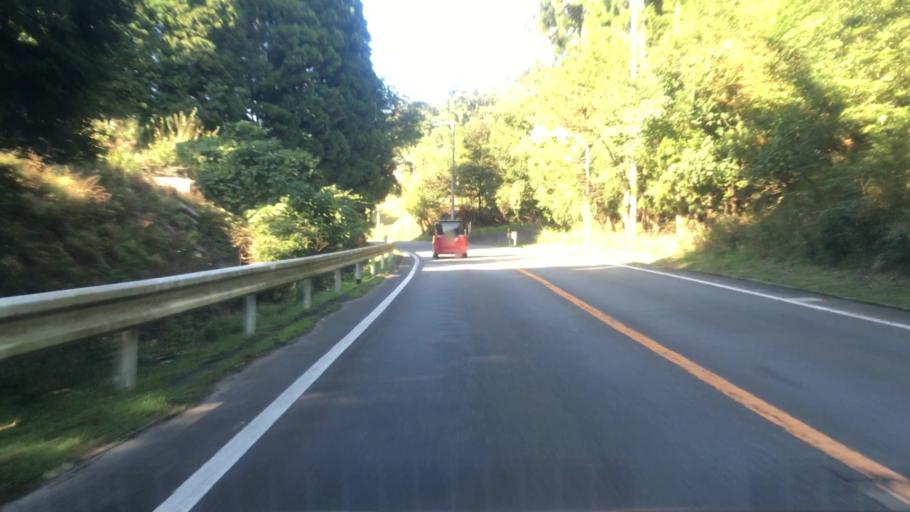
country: JP
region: Hyogo
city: Toyooka
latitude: 35.5655
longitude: 134.8527
